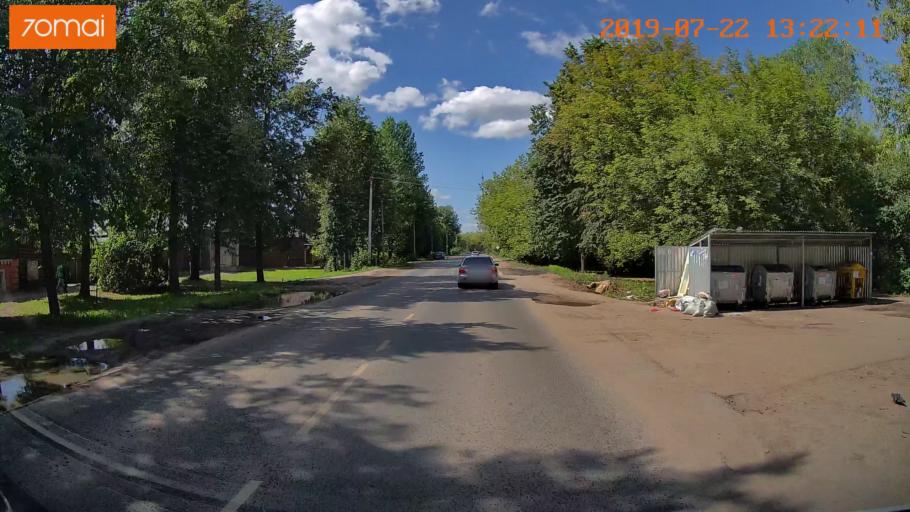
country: RU
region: Ivanovo
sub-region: Gorod Ivanovo
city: Ivanovo
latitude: 57.0229
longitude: 40.9604
